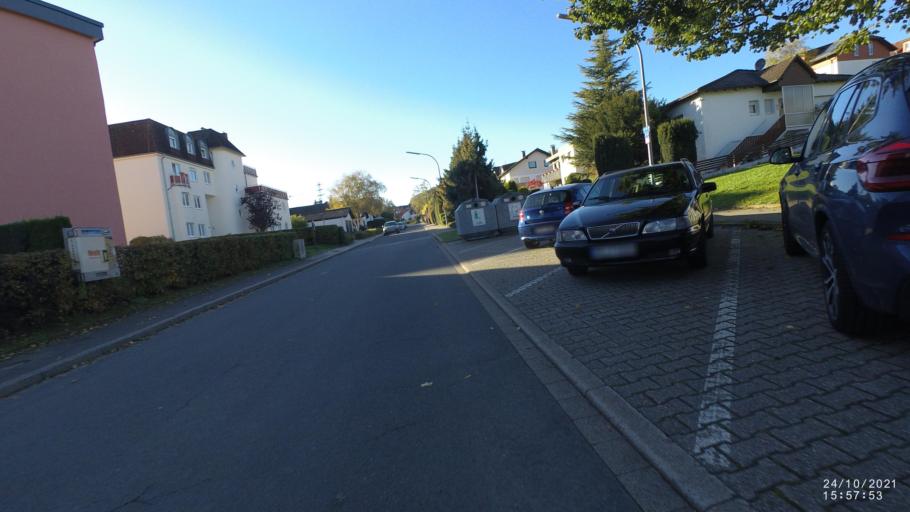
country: DE
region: North Rhine-Westphalia
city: Hemer
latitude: 51.3872
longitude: 7.7534
